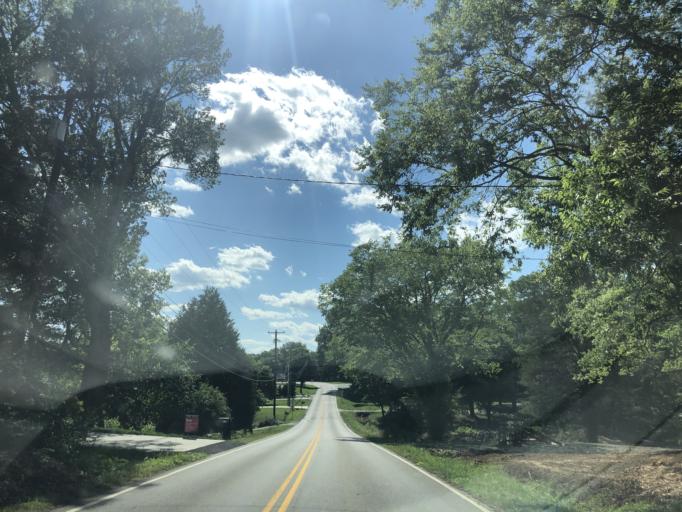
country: US
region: Tennessee
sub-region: Davidson County
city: Belle Meade
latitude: 36.0630
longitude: -86.9299
